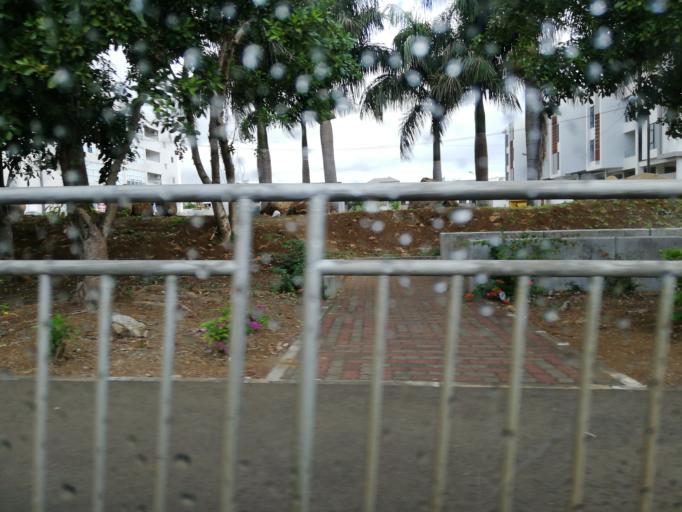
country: MU
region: Plaines Wilhems
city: Ebene
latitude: -20.2418
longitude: 57.4830
